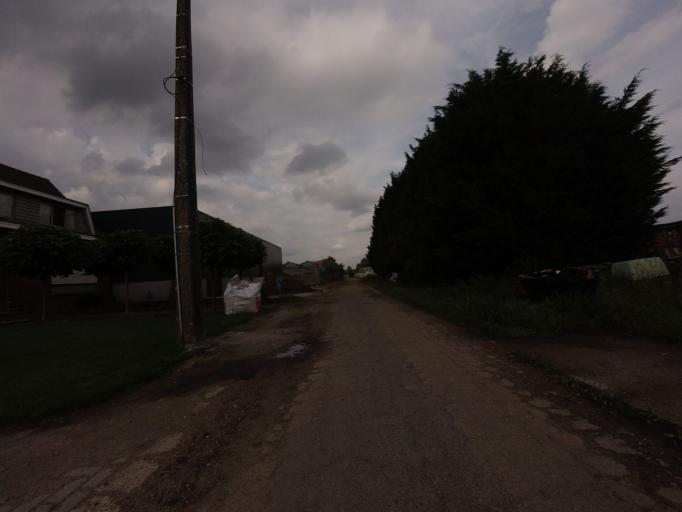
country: BE
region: Flanders
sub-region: Provincie Antwerpen
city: Duffel
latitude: 51.1058
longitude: 4.5004
